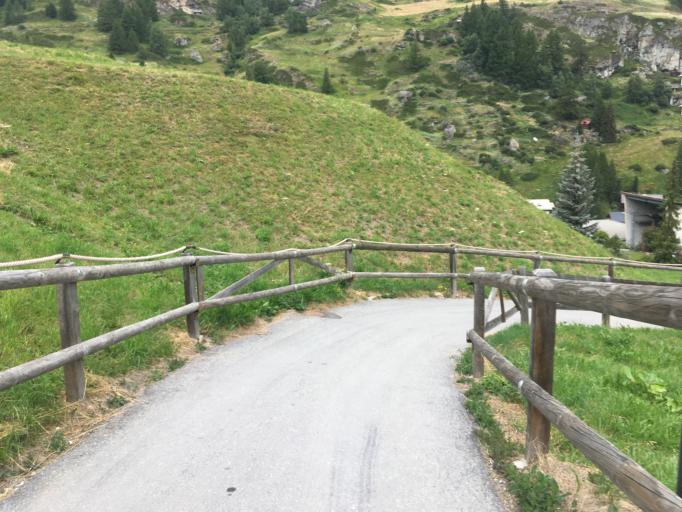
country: CH
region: Valais
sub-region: Visp District
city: Zermatt
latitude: 46.0138
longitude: 7.7437
